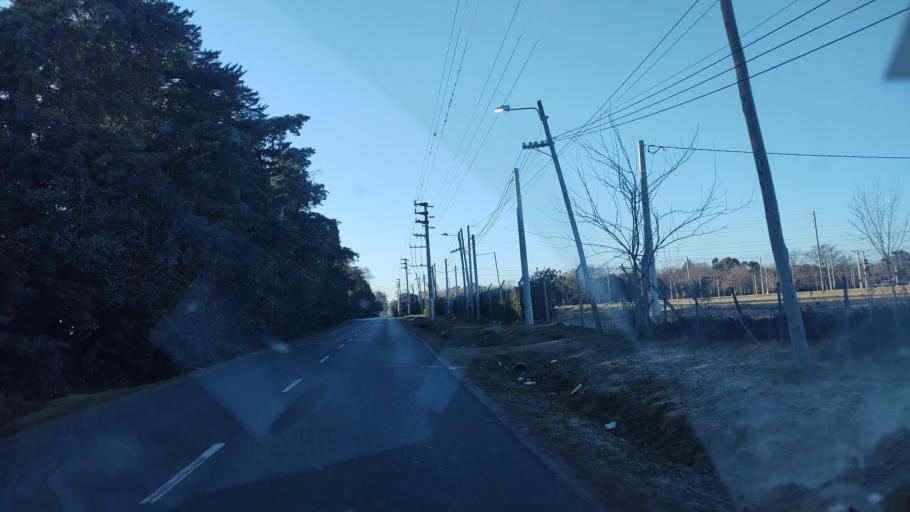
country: AR
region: Buenos Aires
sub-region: Partido de La Plata
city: La Plata
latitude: -34.8991
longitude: -58.0660
